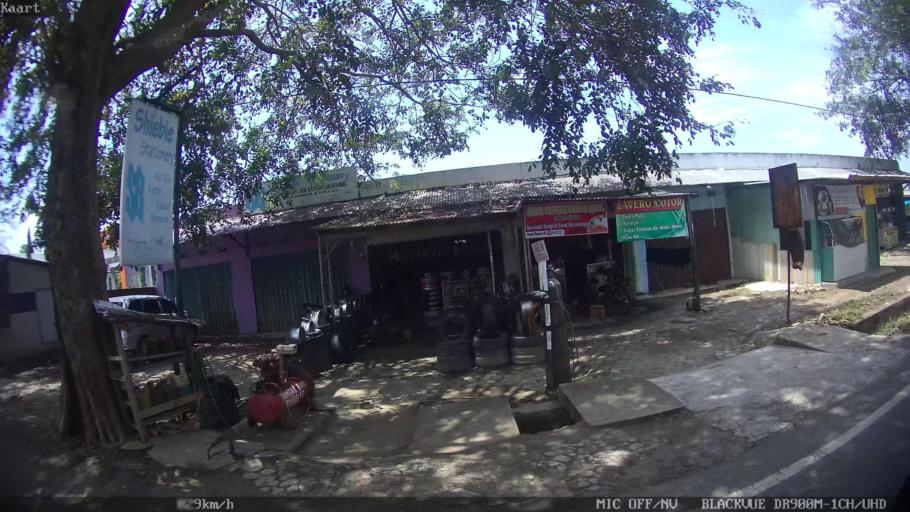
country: ID
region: Lampung
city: Kedaton
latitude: -5.3591
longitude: 105.2843
